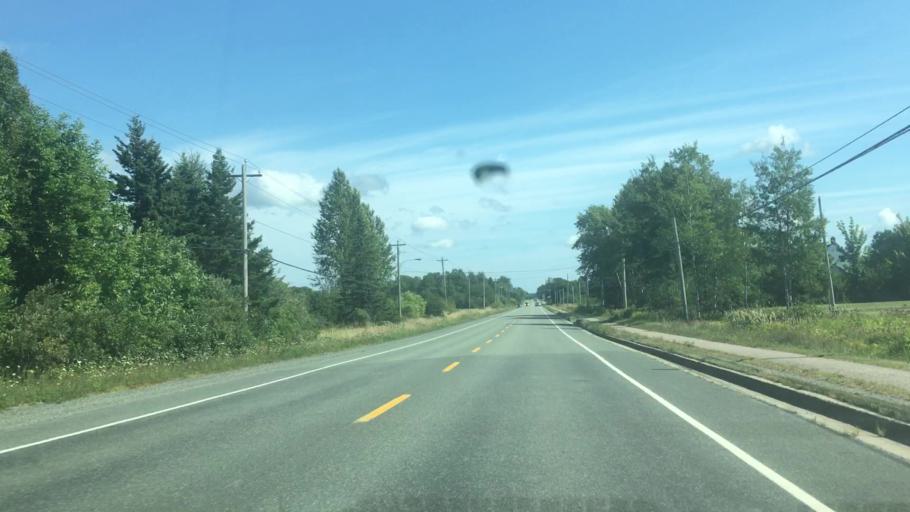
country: CA
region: Nova Scotia
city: Sydney
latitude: 46.0558
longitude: -60.3121
